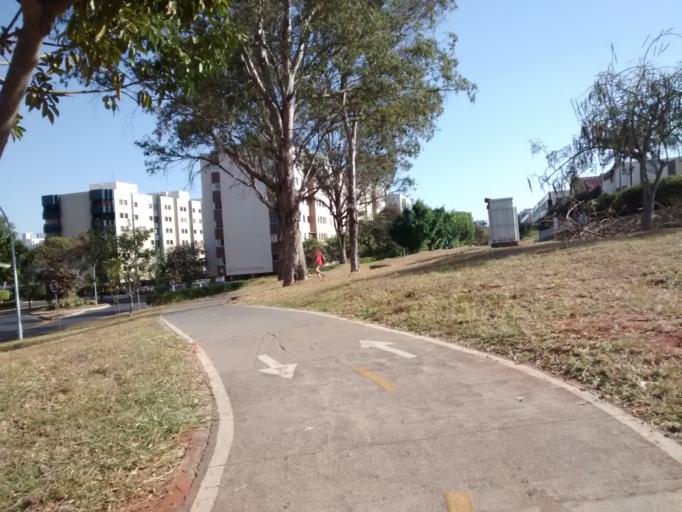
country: BR
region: Federal District
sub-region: Brasilia
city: Brasilia
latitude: -15.8025
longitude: -47.9268
